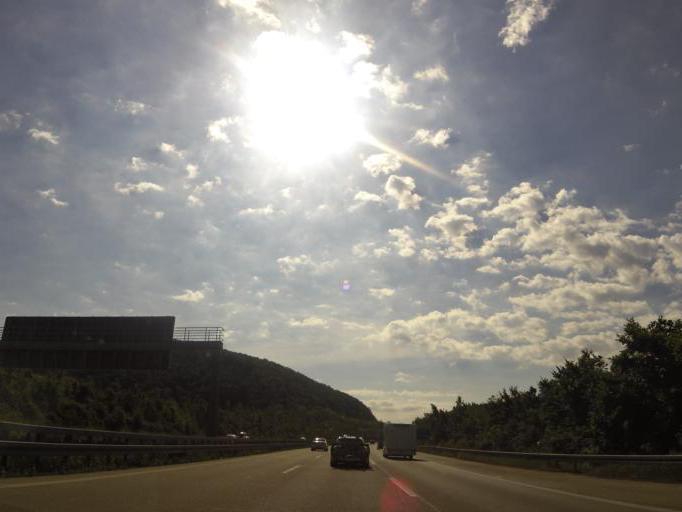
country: DE
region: Baden-Wuerttemberg
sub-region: Regierungsbezirk Stuttgart
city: Aichelberg
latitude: 48.6327
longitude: 9.5615
